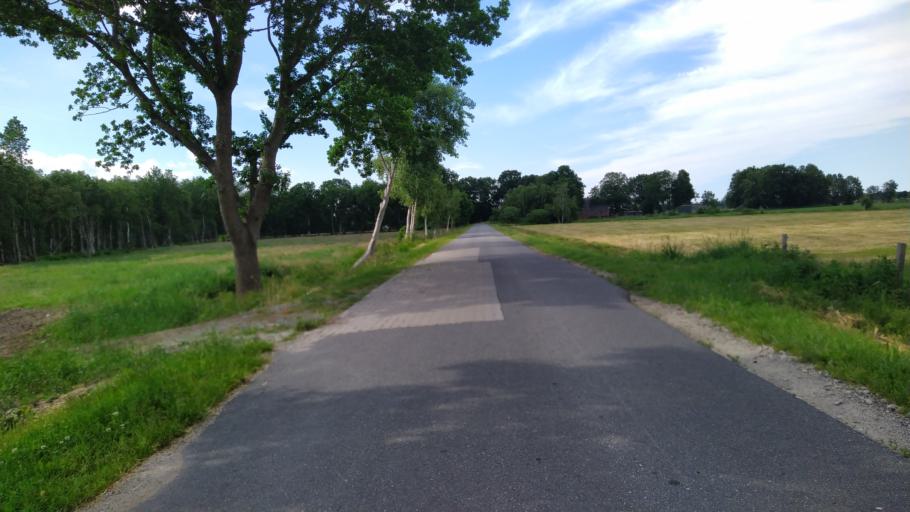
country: DE
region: Lower Saxony
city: Odisheim
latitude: 53.6555
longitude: 8.9354
